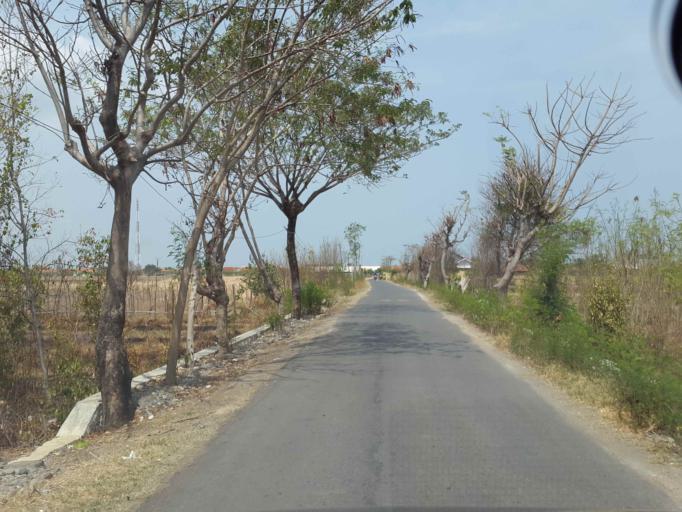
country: ID
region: Central Java
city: Dukuhturi
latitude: -6.8278
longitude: 109.0531
